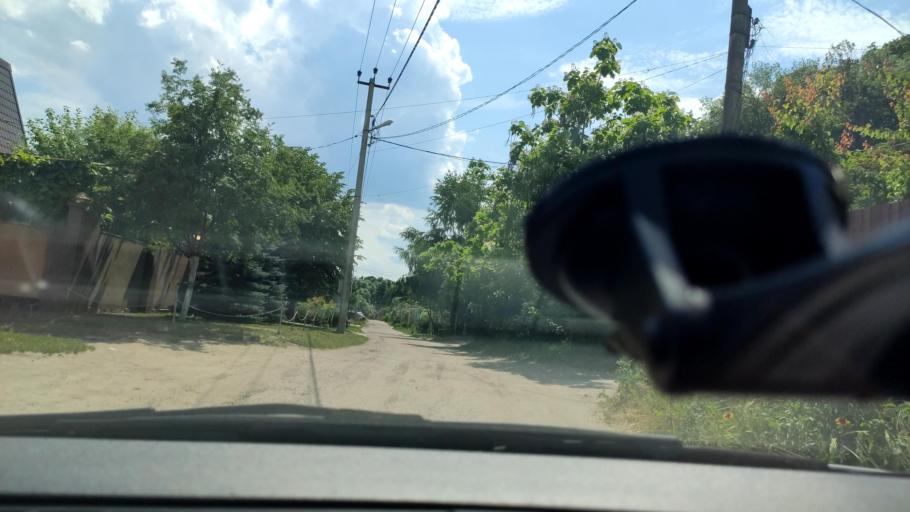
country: RU
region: Voronezj
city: Ramon'
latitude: 51.8933
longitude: 39.3431
